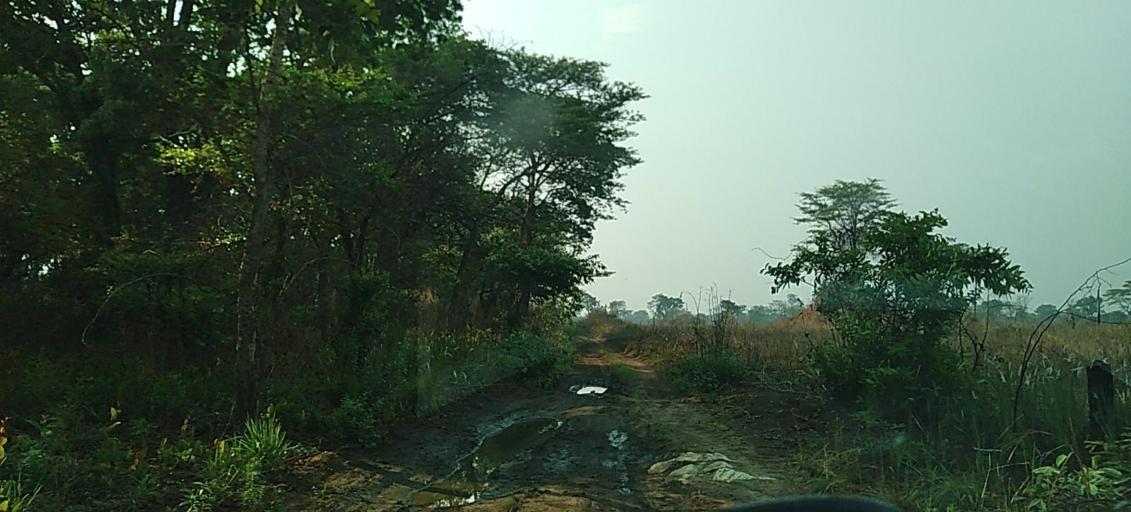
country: ZM
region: North-Western
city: Solwezi
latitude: -12.3754
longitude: 26.5616
